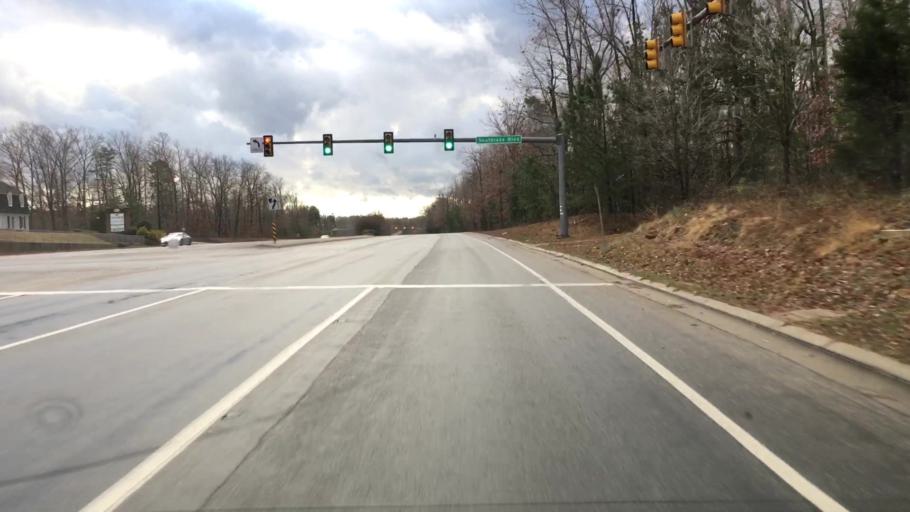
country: US
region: Virginia
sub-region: Chesterfield County
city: Bon Air
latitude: 37.4993
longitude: -77.6083
